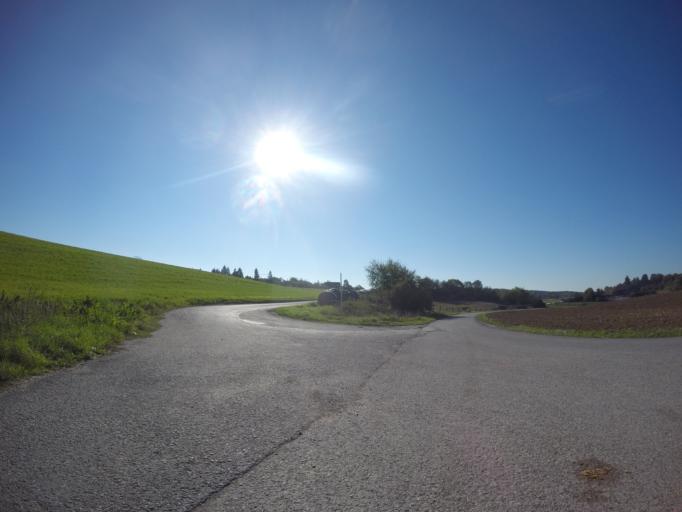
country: DE
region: Bavaria
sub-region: Regierungsbezirk Unterfranken
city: Remlingen
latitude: 49.8102
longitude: 9.6894
